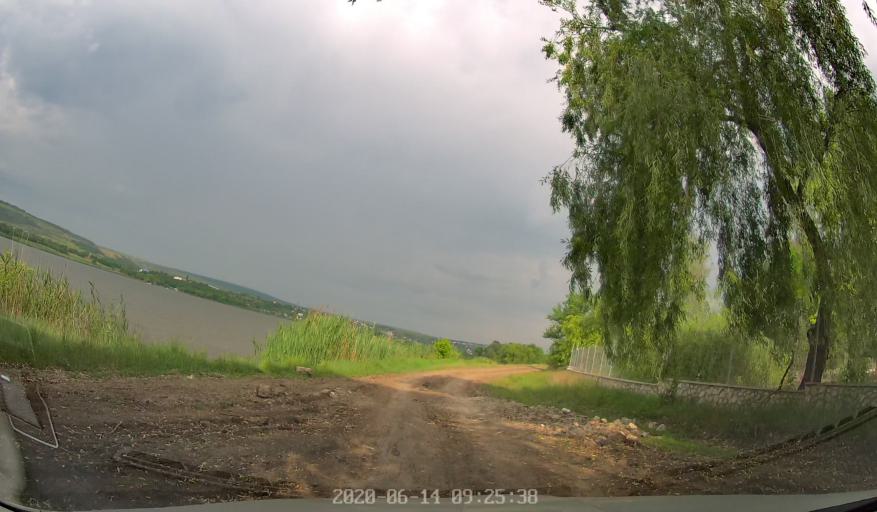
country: MD
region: Laloveni
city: Ialoveni
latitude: 46.9827
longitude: 28.7039
